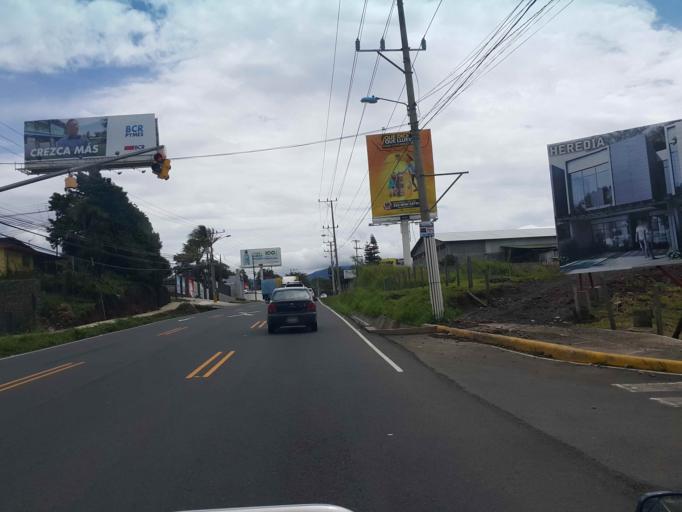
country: CR
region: Heredia
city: San Pablo
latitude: 9.9775
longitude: -84.1113
